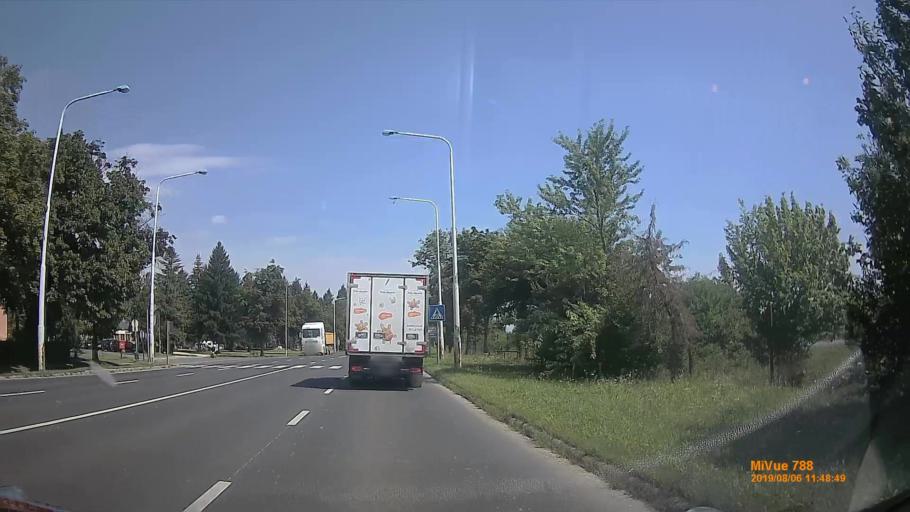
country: HU
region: Vas
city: Kormend
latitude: 47.0158
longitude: 16.6114
